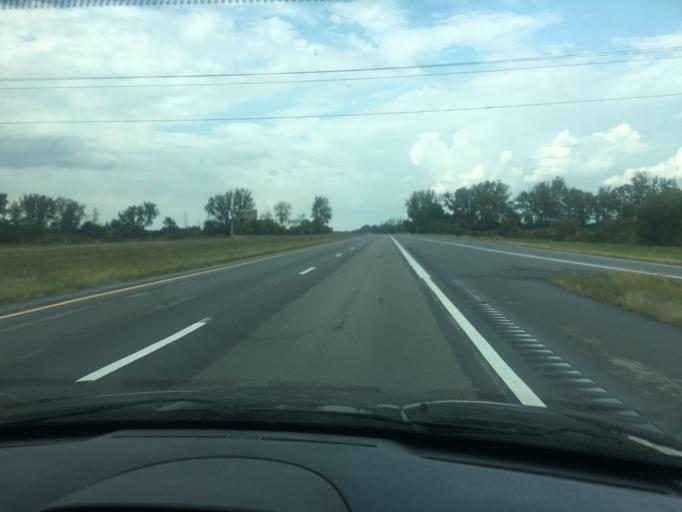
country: US
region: Ohio
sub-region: Clark County
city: Northridge
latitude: 39.9896
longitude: -83.8123
